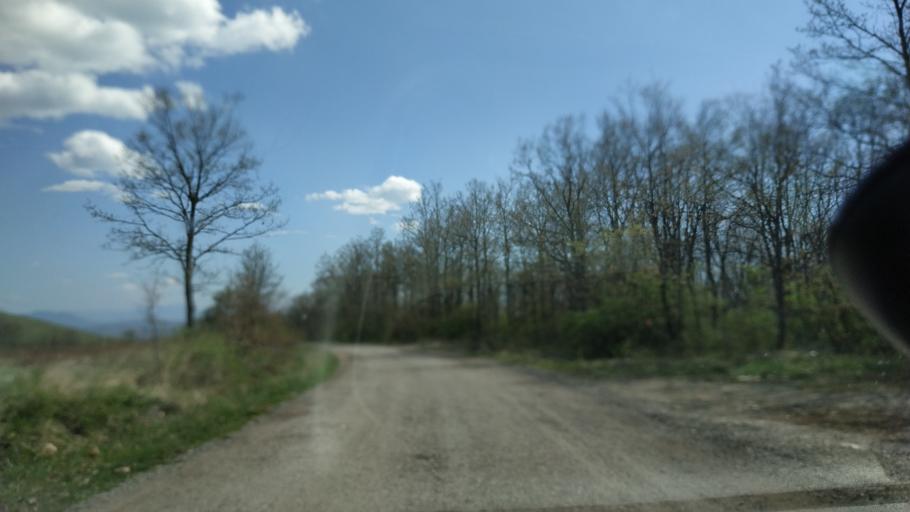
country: RS
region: Central Serbia
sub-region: Zajecarski Okrug
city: Soko Banja
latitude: 43.5458
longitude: 21.9007
